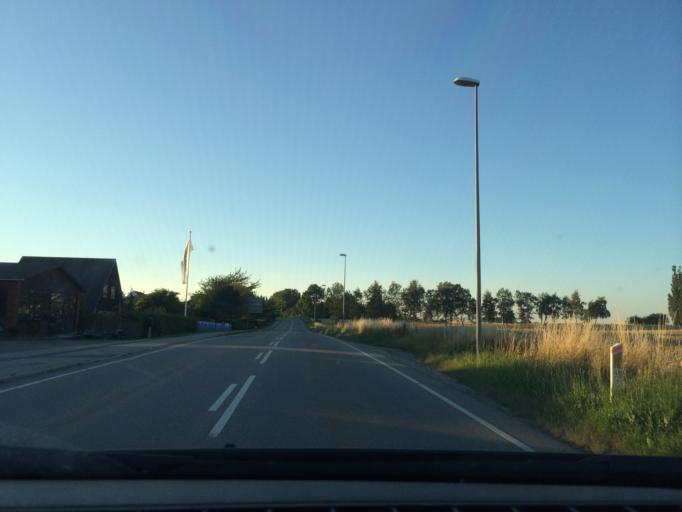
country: DK
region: Zealand
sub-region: Vordingborg Kommune
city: Stege
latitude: 54.9986
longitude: 12.1580
